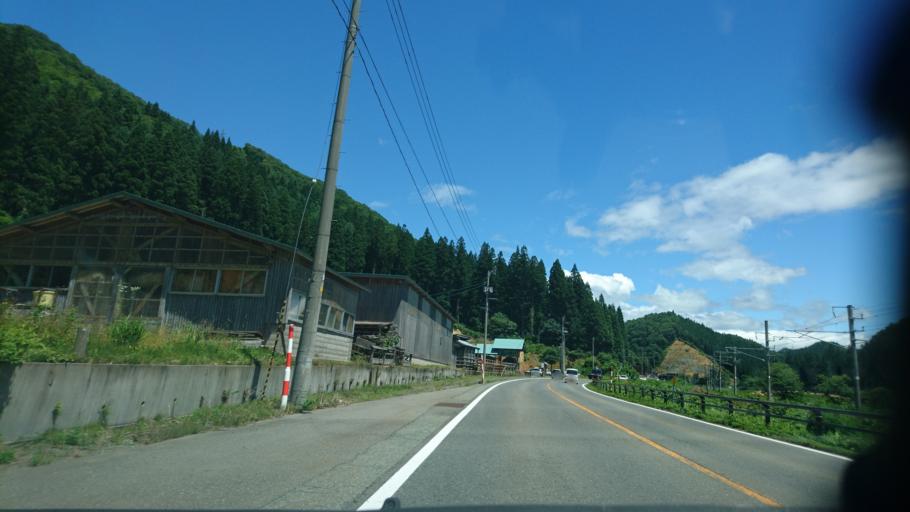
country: JP
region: Akita
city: Kakunodatemachi
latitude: 39.6467
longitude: 140.6646
